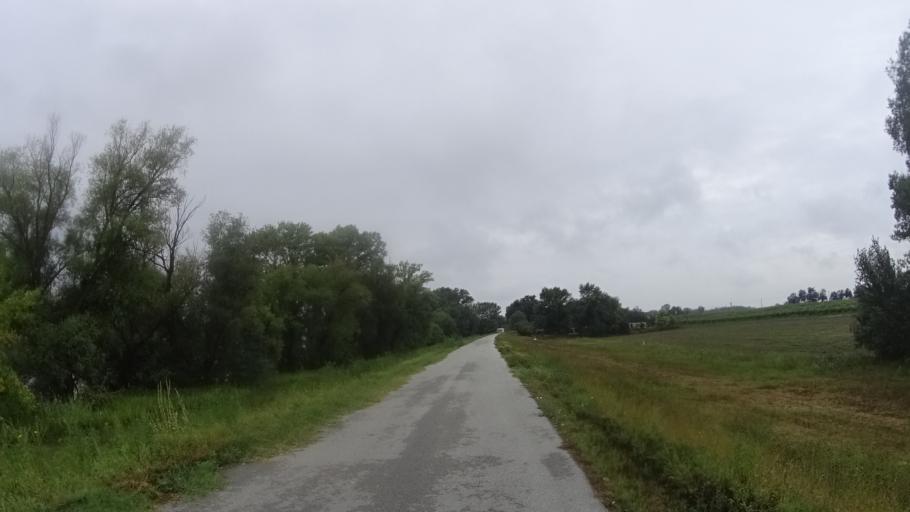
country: HU
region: Komarom-Esztergom
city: Neszmely
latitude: 47.7538
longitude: 18.3976
